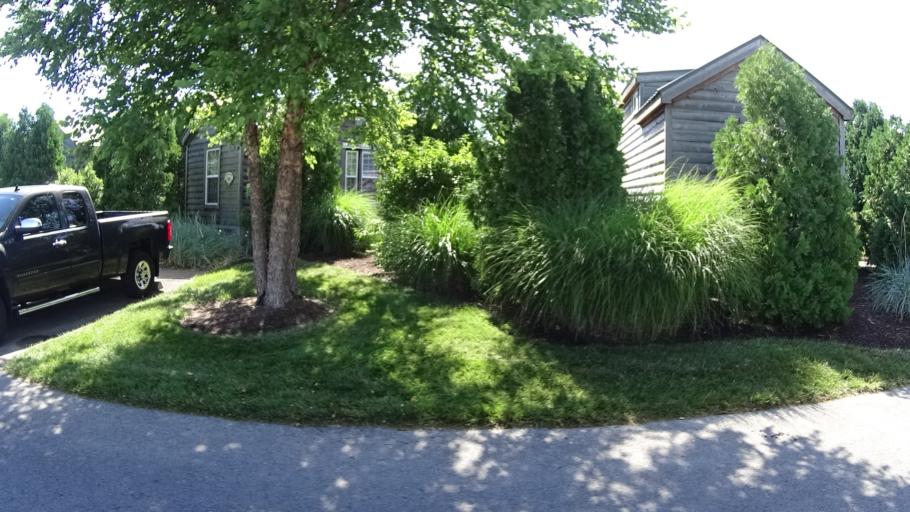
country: US
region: Ohio
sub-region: Erie County
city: Sandusky
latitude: 41.4900
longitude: -82.6907
